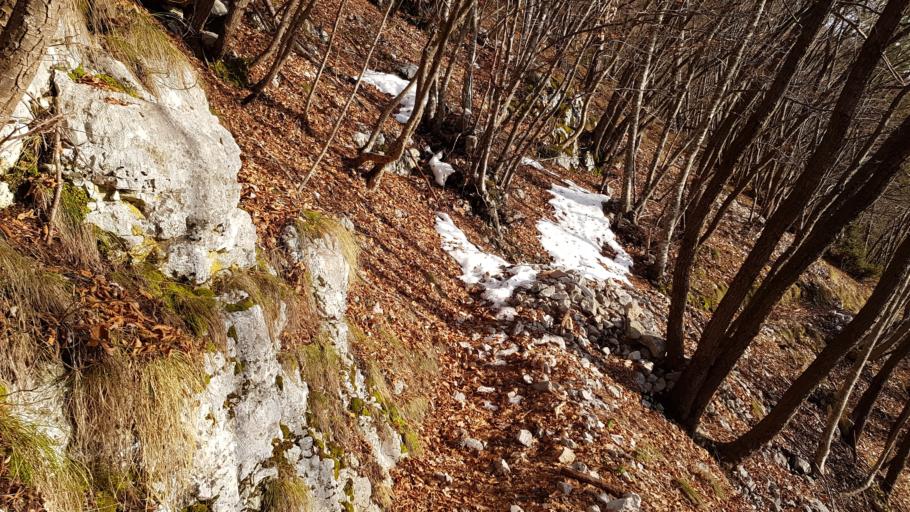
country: IT
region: Trentino-Alto Adige
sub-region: Provincia di Trento
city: Padergnone
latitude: 46.0720
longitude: 10.9520
